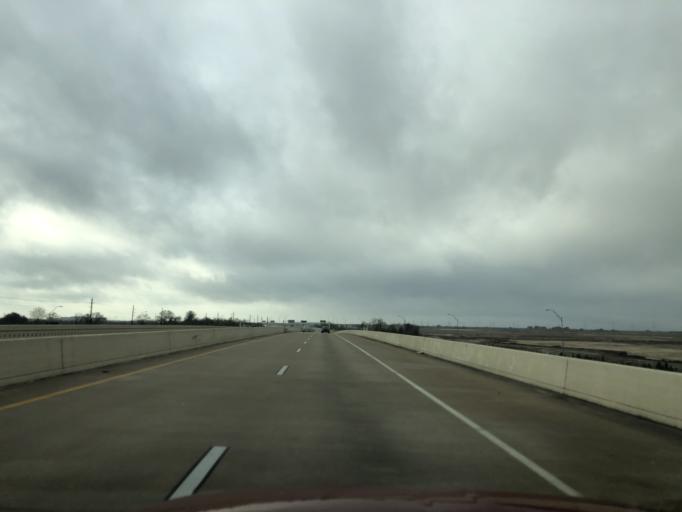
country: US
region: Texas
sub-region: Harris County
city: Cypress
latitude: 29.9540
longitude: -95.7698
